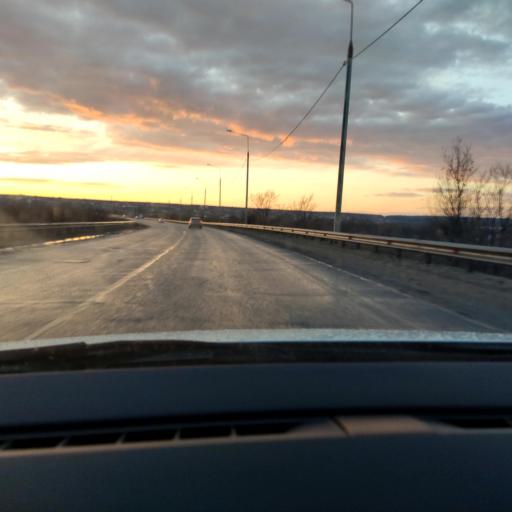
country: RU
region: Voronezj
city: Pridonskoy
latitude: 51.7201
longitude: 39.0700
